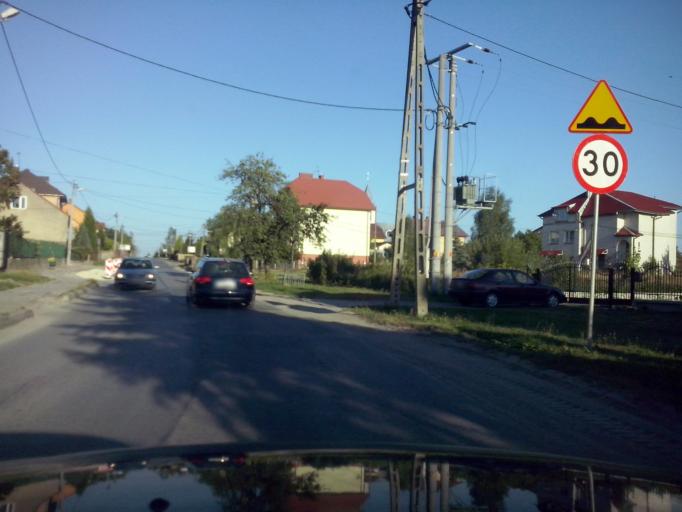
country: PL
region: Swietokrzyskie
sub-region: Powiat kielecki
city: Kielce
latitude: 50.8192
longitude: 20.6256
